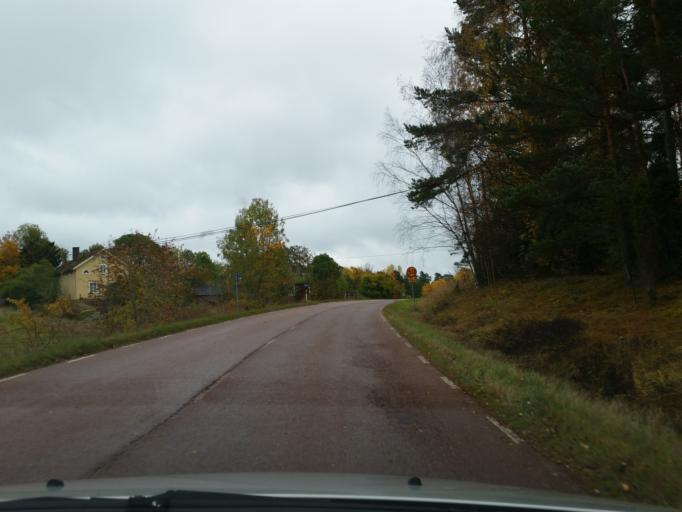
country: AX
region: Alands landsbygd
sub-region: Lumparland
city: Lumparland
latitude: 60.1162
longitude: 20.2602
